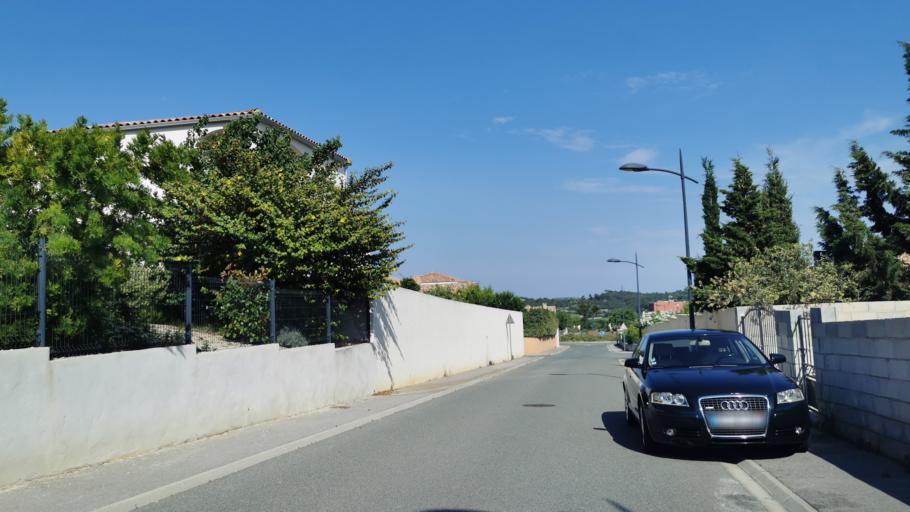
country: FR
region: Languedoc-Roussillon
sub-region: Departement de l'Aude
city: Peyriac-de-Mer
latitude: 43.1350
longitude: 2.9595
